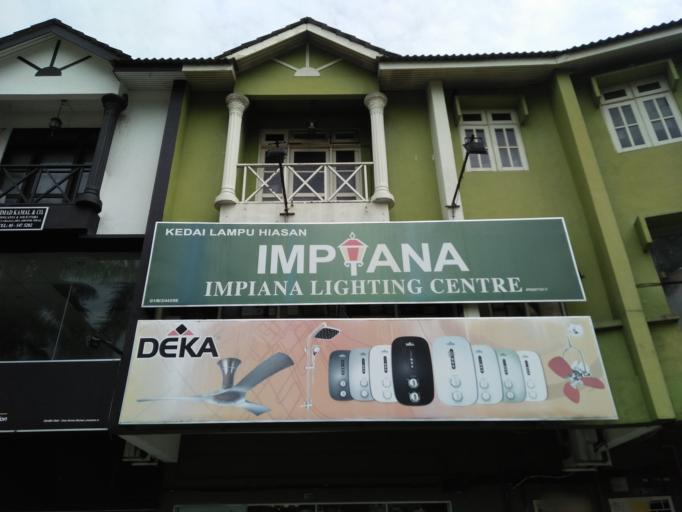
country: MY
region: Perak
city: Ipoh
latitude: 4.6106
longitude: 101.1003
